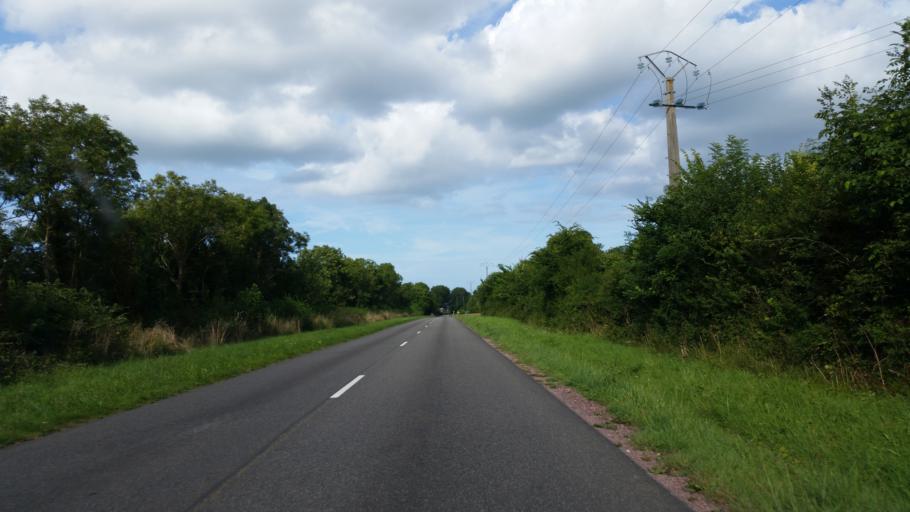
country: FR
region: Lower Normandy
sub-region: Departement de la Manche
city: Sainte-Mere-Eglise
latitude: 49.4510
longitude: -1.2745
